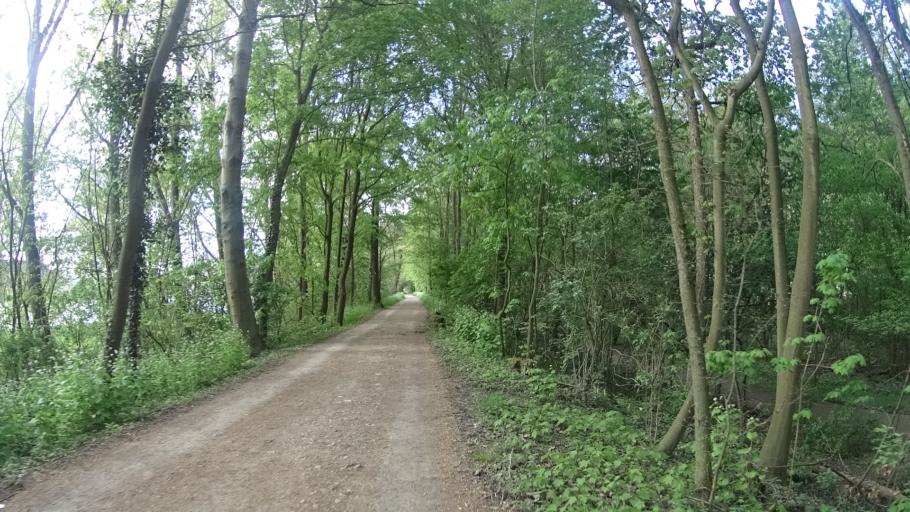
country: DE
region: Rheinland-Pfalz
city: Koblenz
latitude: 50.3271
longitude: 7.5883
